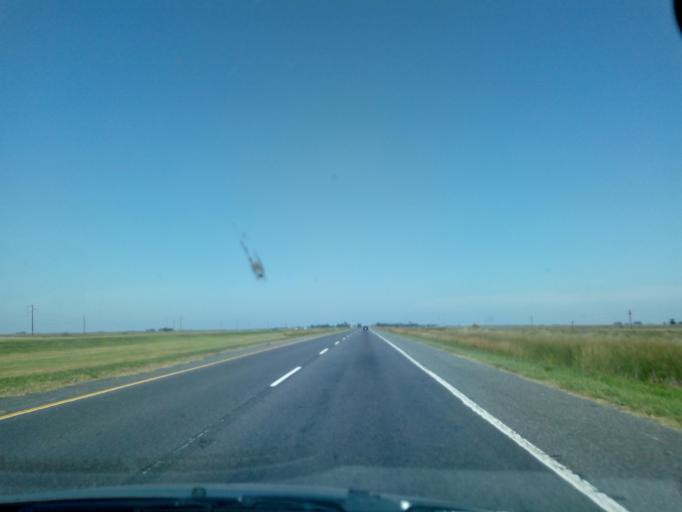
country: AR
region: Buenos Aires
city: Maipu
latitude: -36.9588
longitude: -57.8682
